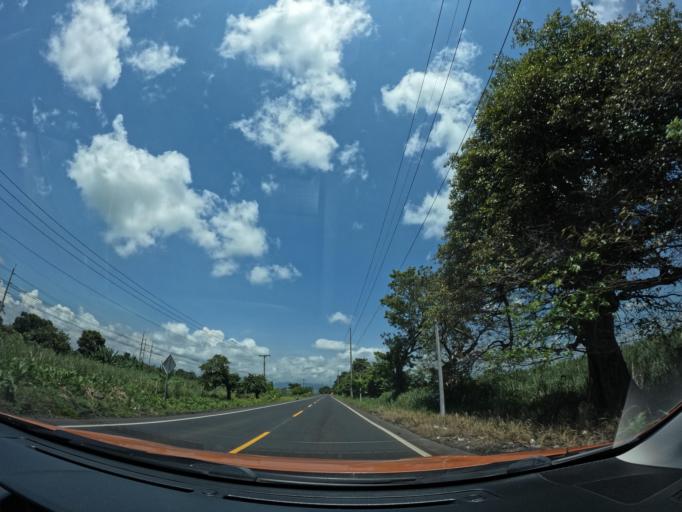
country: GT
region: Escuintla
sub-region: Municipio de Masagua
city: Masagua
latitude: 14.2385
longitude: -90.8181
